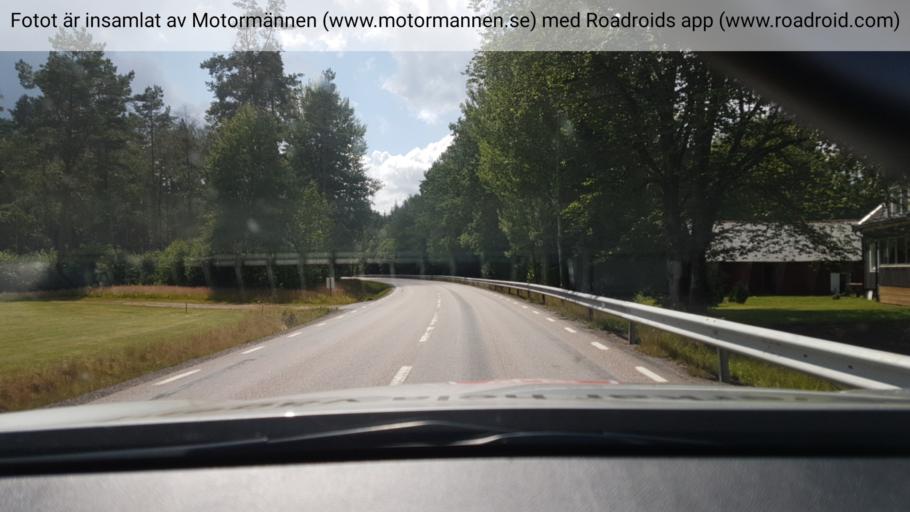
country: SE
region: Vaestra Goetaland
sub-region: Svenljunga Kommun
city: Svenljunga
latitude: 57.4927
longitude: 13.0672
